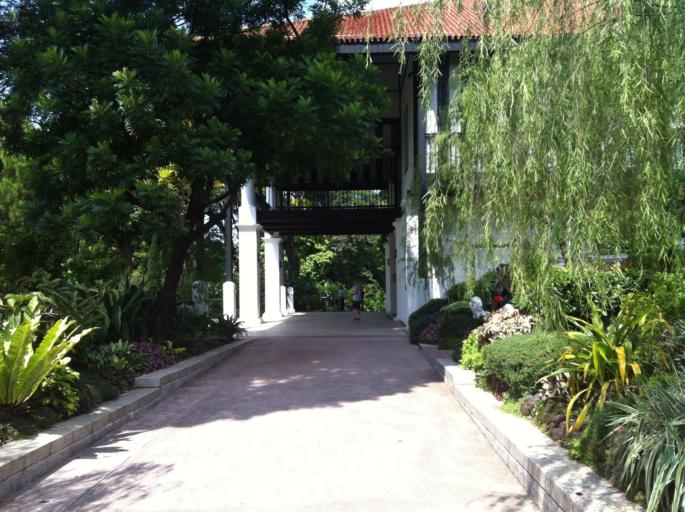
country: SG
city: Singapore
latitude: 1.3125
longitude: 103.8138
